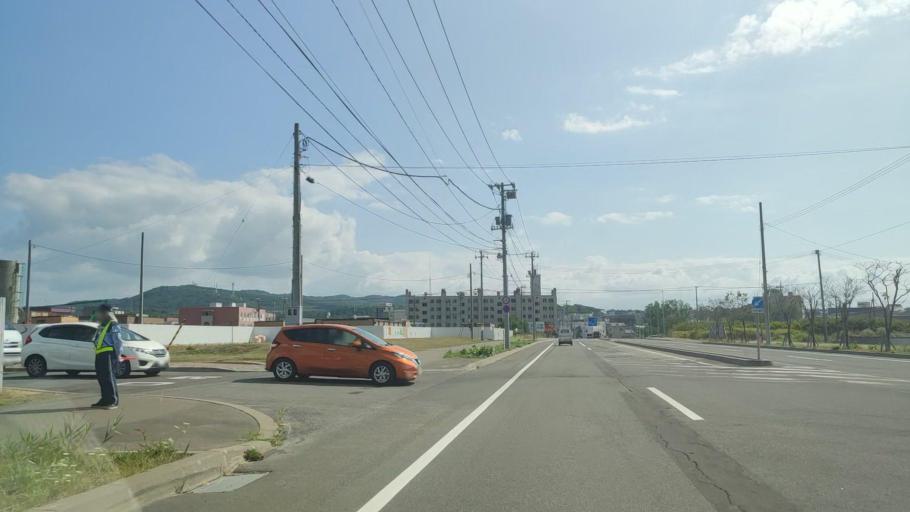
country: JP
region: Hokkaido
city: Rumoi
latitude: 43.9445
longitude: 141.6479
